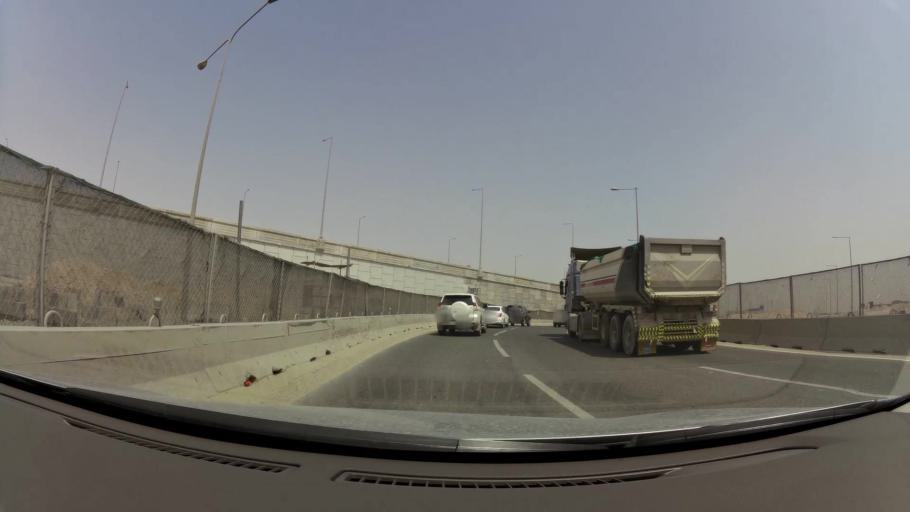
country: QA
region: Al Wakrah
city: Al Wukayr
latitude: 25.1924
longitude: 51.4566
